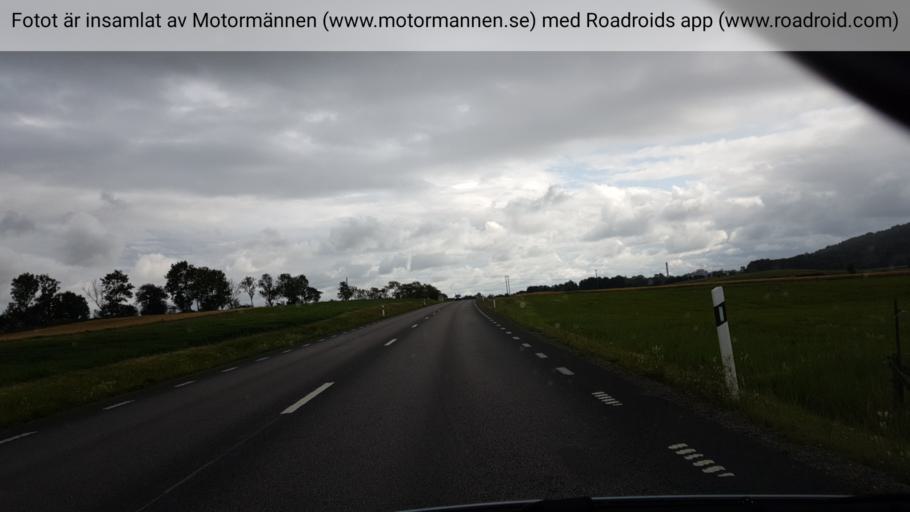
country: SE
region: Vaestra Goetaland
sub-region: Falkopings Kommun
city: Falkoeping
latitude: 58.2015
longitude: 13.5604
